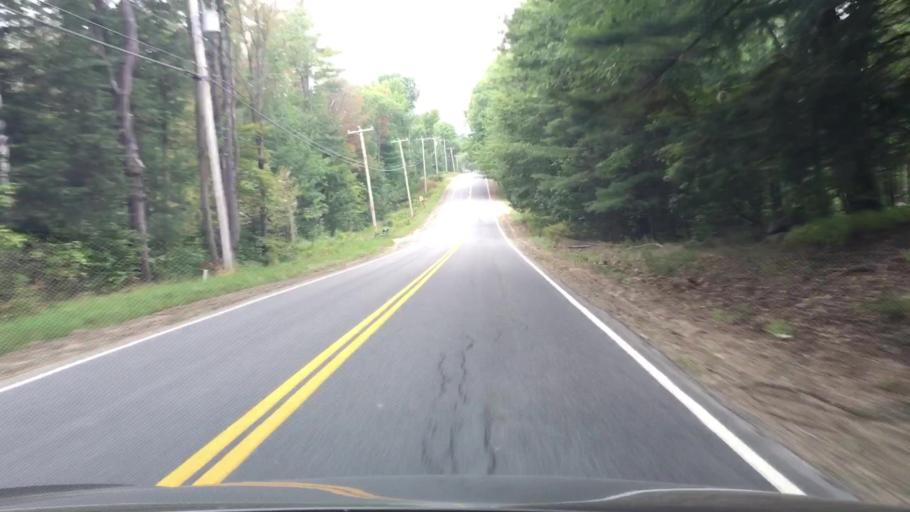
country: US
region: Maine
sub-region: Androscoggin County
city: Livermore
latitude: 44.3344
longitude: -70.2258
